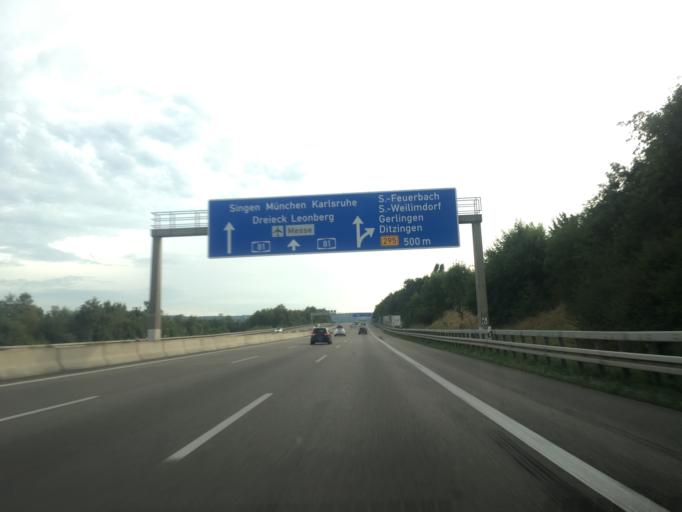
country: DE
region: Baden-Wuerttemberg
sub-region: Regierungsbezirk Stuttgart
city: Ditzingen
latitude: 48.8277
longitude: 9.0827
